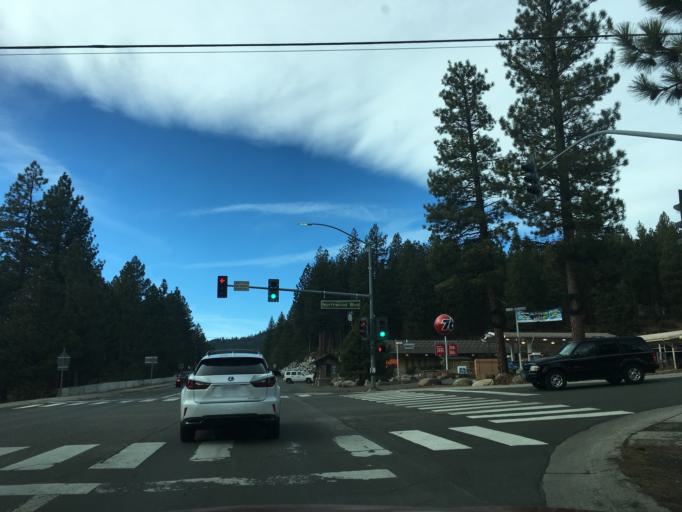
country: US
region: Nevada
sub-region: Washoe County
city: Incline Village
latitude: 39.2504
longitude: -119.9615
